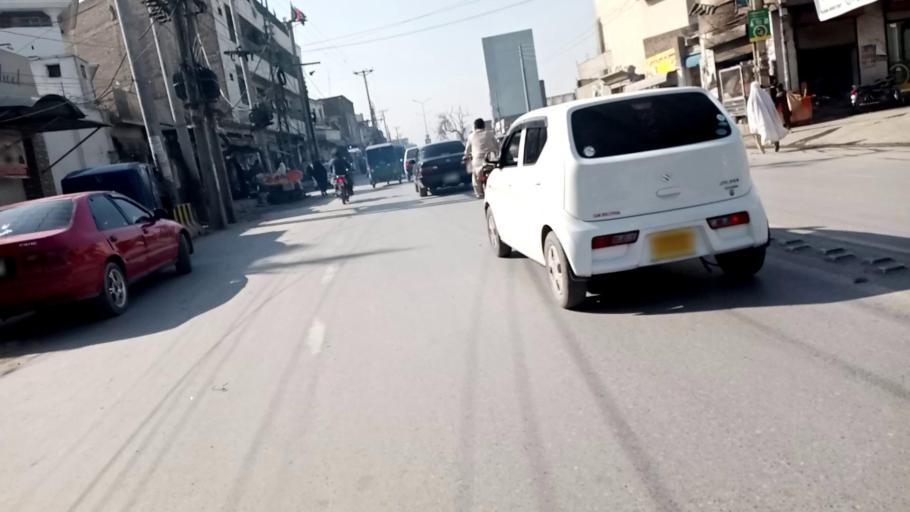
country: PK
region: Khyber Pakhtunkhwa
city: Peshawar
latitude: 33.9804
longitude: 71.5231
